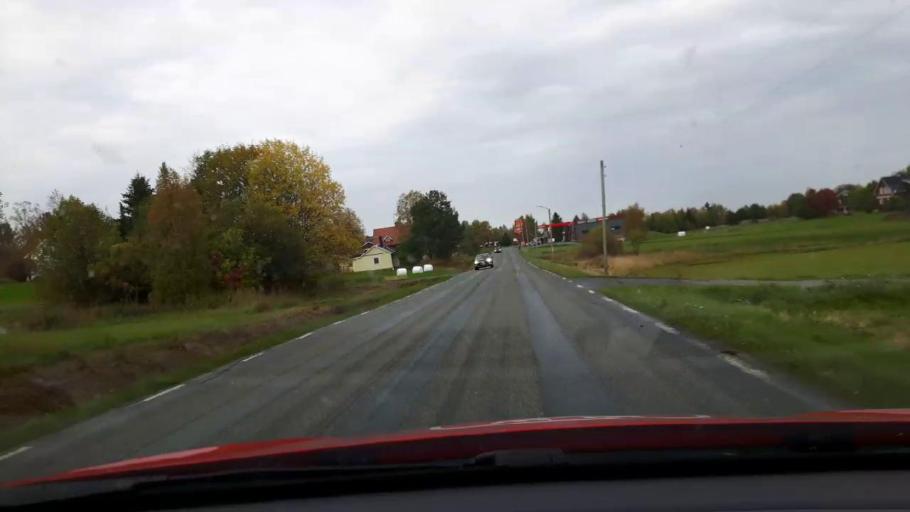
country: SE
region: Jaemtland
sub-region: Bergs Kommun
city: Hoverberg
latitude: 62.8365
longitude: 14.3845
